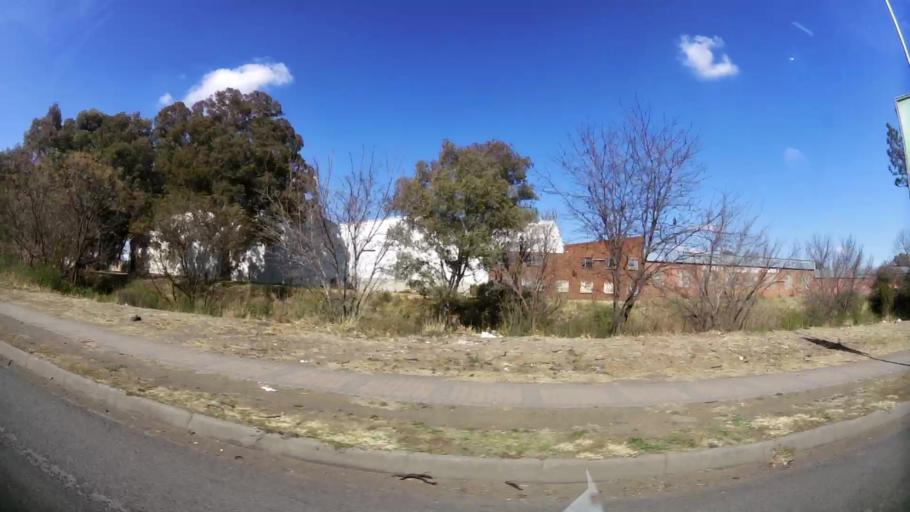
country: ZA
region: Orange Free State
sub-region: Mangaung Metropolitan Municipality
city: Bloemfontein
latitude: -29.1195
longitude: 26.2317
